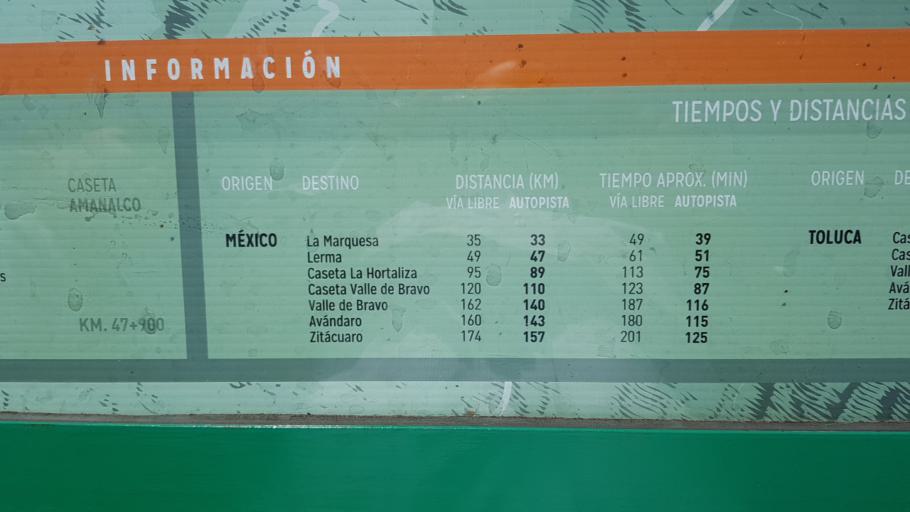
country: MX
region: Mexico
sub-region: Almoloya de Juarez
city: San Pedro de la Hortaliza (Ejido Almoloyan)
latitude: 19.3801
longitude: -99.8199
